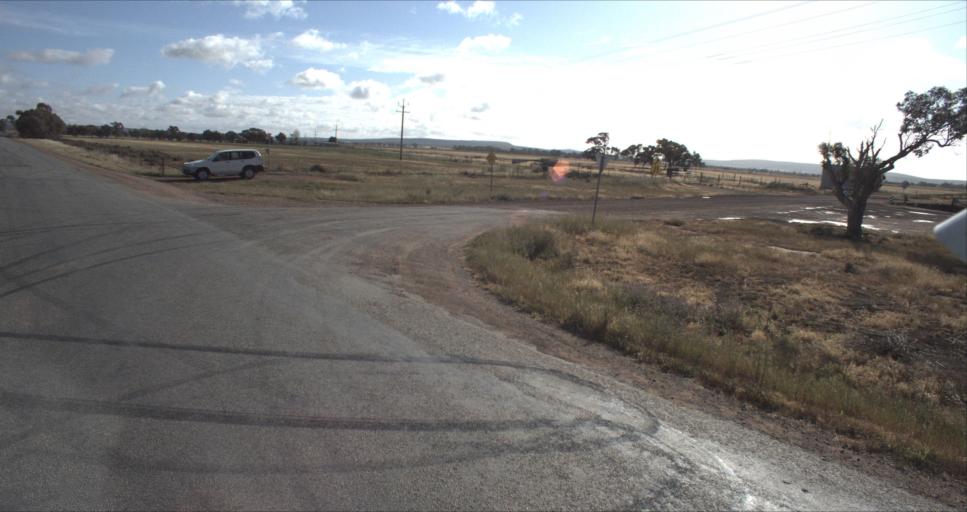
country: AU
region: New South Wales
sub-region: Leeton
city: Leeton
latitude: -34.5113
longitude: 146.3922
